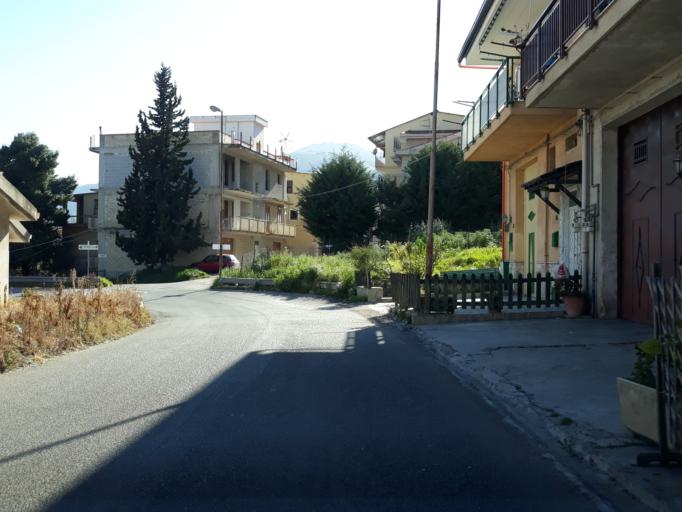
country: IT
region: Sicily
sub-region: Palermo
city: Misilmeri
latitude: 38.0301
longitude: 13.4406
